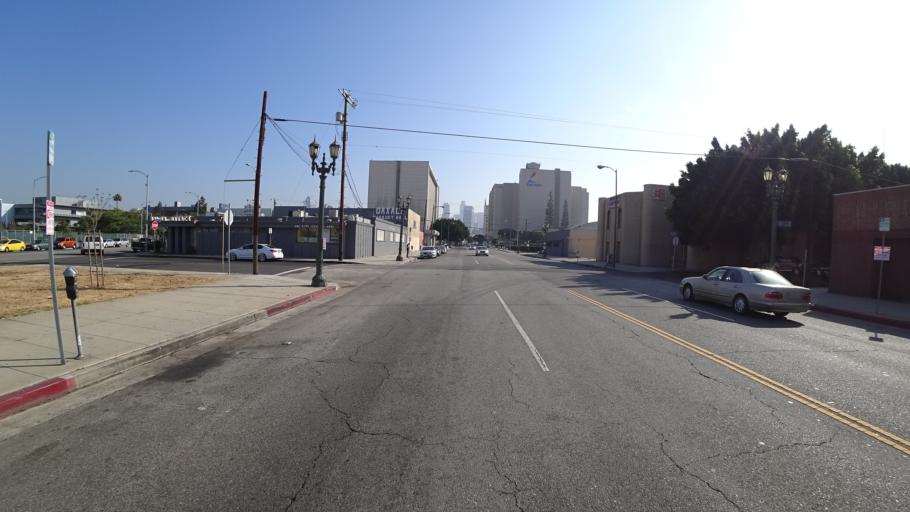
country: US
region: California
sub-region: Los Angeles County
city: Los Angeles
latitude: 34.0292
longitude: -118.2687
